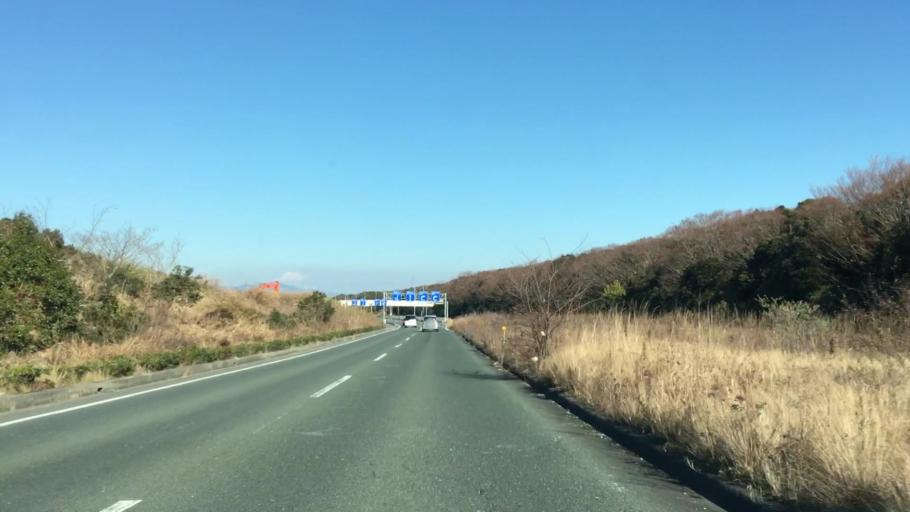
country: JP
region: Aichi
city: Tahara
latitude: 34.6951
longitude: 137.3236
